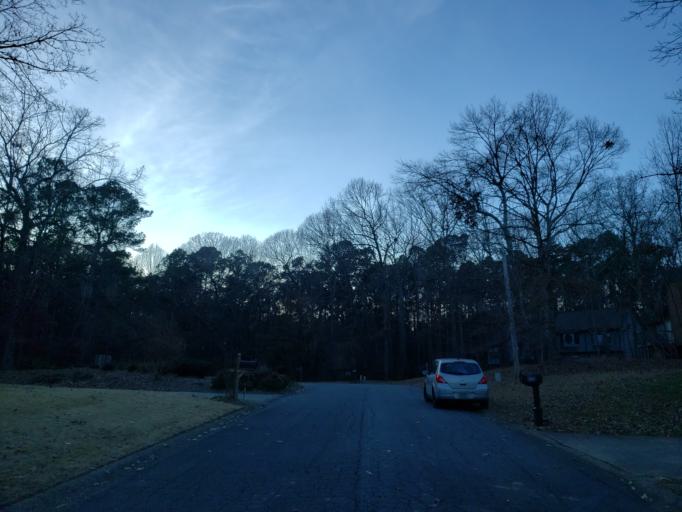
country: US
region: Georgia
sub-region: Cobb County
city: Acworth
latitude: 34.0474
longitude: -84.6498
